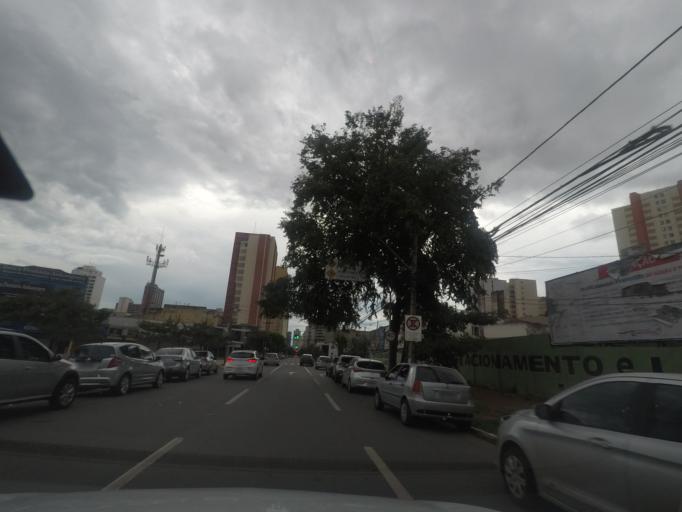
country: BR
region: Goias
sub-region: Goiania
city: Goiania
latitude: -16.6770
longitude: -49.2611
